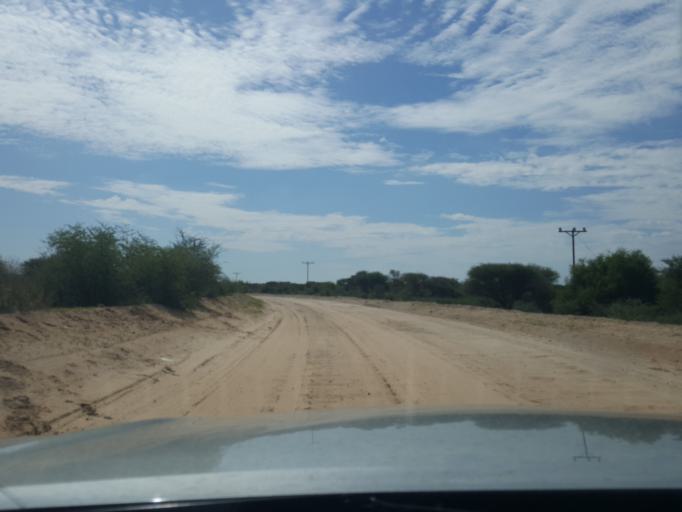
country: BW
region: Kweneng
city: Letlhakeng
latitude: -24.0547
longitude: 25.0302
